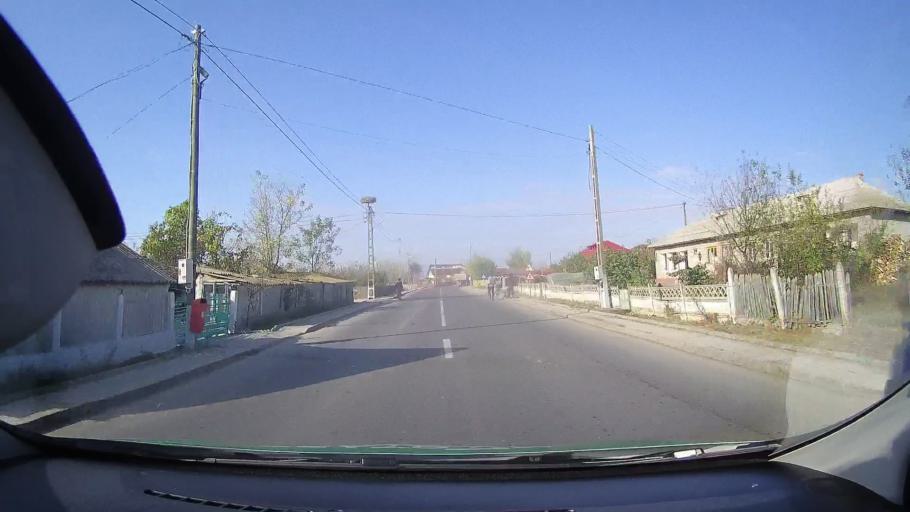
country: RO
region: Tulcea
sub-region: Comuna Mahmudia
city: Mahmudia
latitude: 45.0087
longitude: 29.0568
